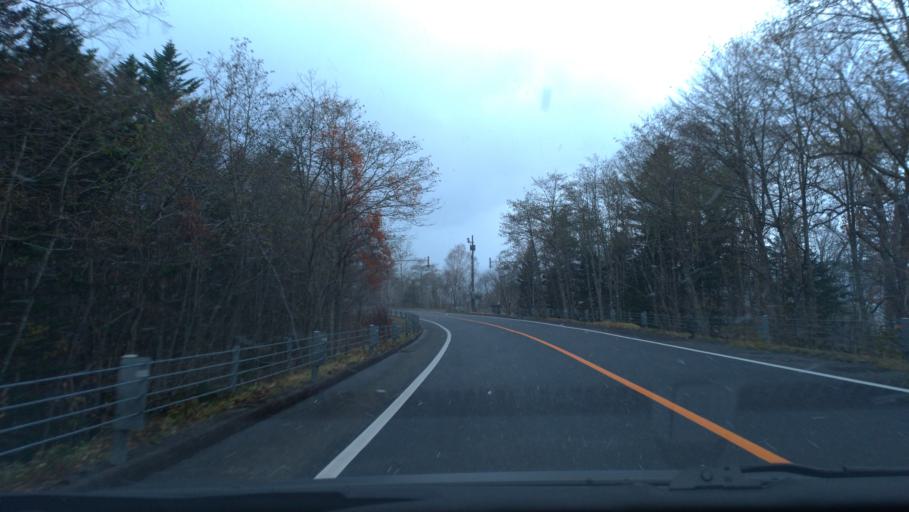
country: JP
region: Hokkaido
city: Shiraoi
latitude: 42.7419
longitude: 141.4038
